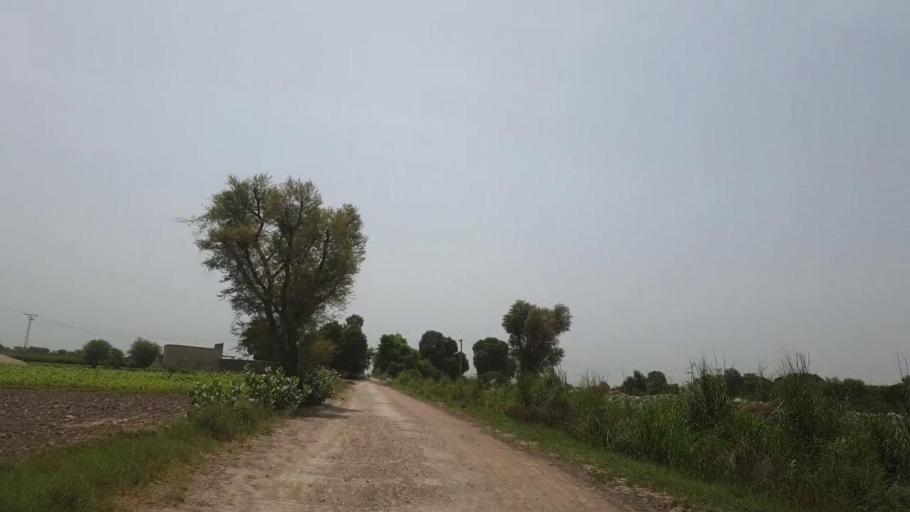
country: PK
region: Sindh
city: Sakrand
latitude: 26.0750
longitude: 68.2652
